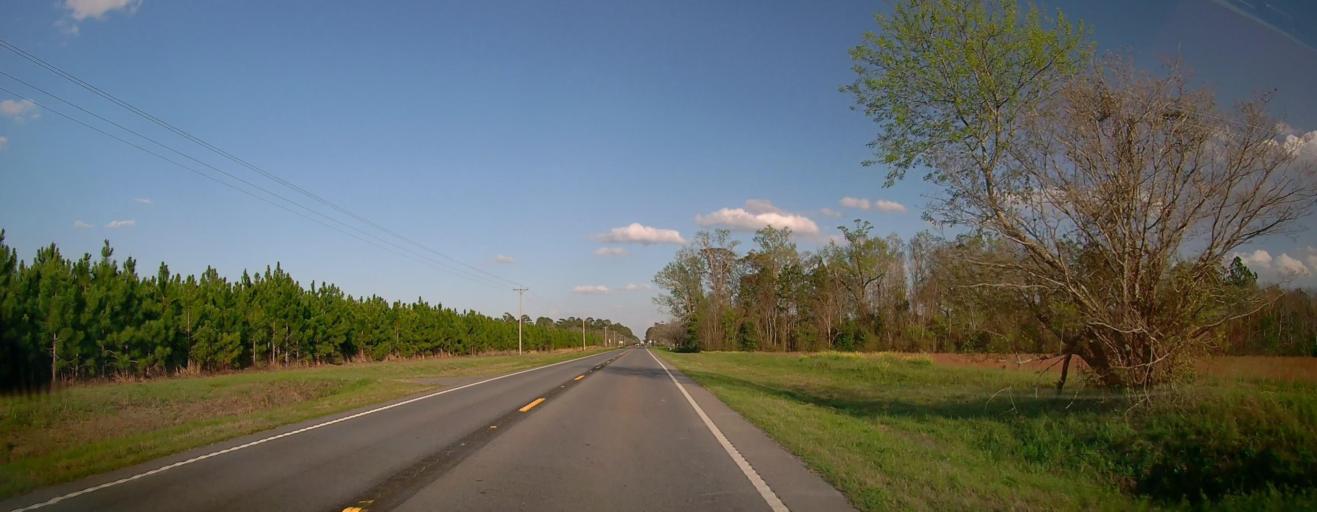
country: US
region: Georgia
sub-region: Evans County
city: Claxton
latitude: 32.1498
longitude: -81.9993
